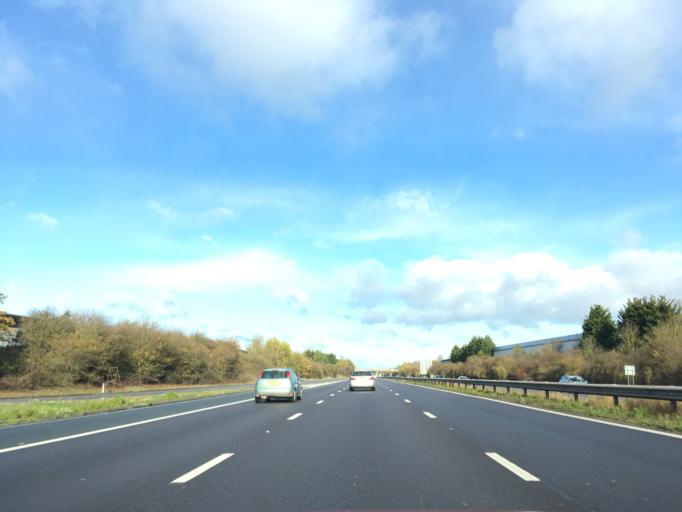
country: GB
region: England
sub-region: Worcestershire
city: Bredon
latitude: 51.9988
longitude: -2.1233
